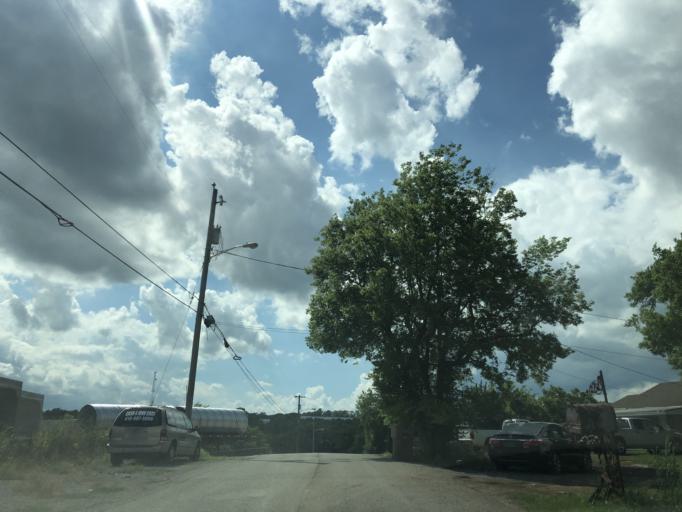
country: US
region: Tennessee
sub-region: Davidson County
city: Nashville
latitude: 36.2160
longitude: -86.7655
